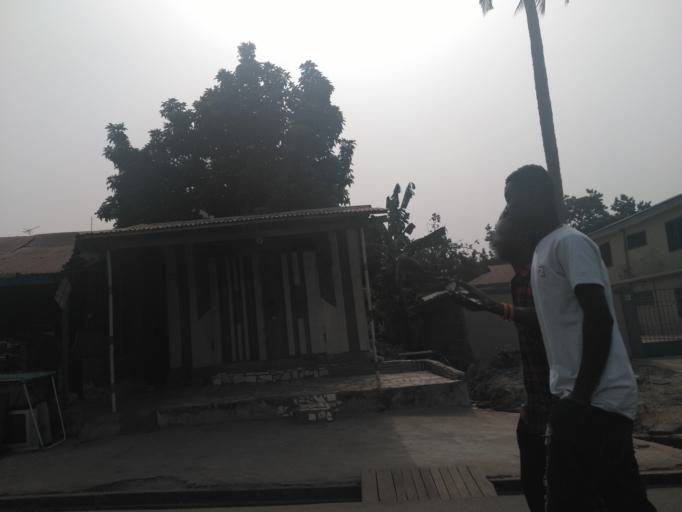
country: GH
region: Ashanti
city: Kumasi
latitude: 6.7109
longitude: -1.6390
